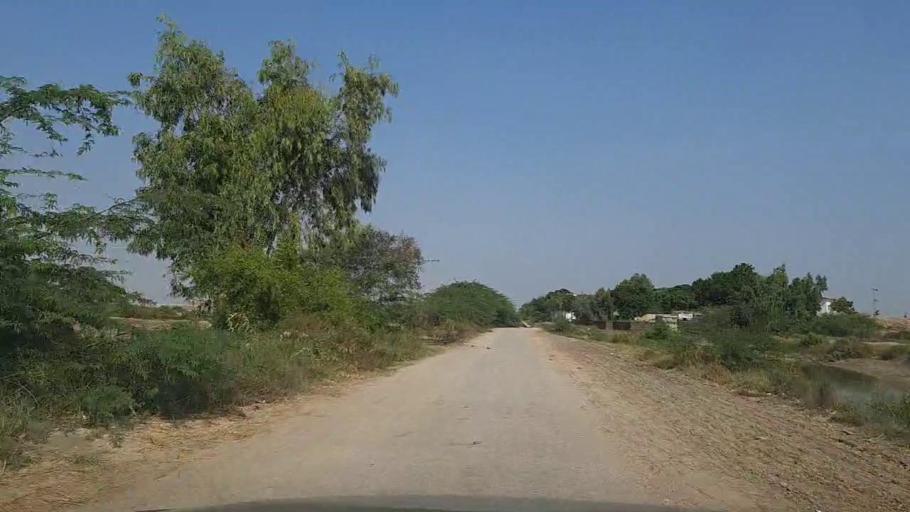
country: PK
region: Sindh
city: Thatta
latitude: 24.6176
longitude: 67.9595
